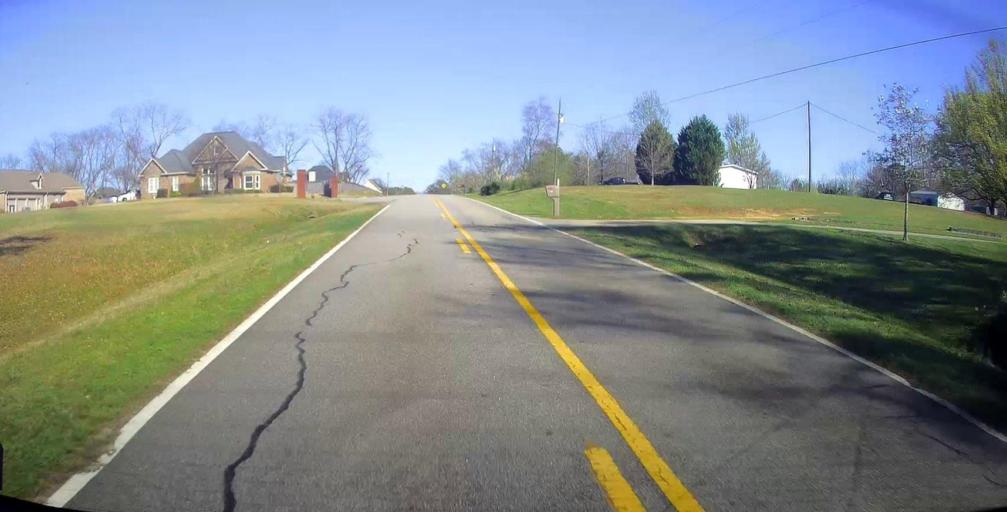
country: US
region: Georgia
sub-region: Peach County
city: Byron
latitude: 32.6447
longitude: -83.7941
